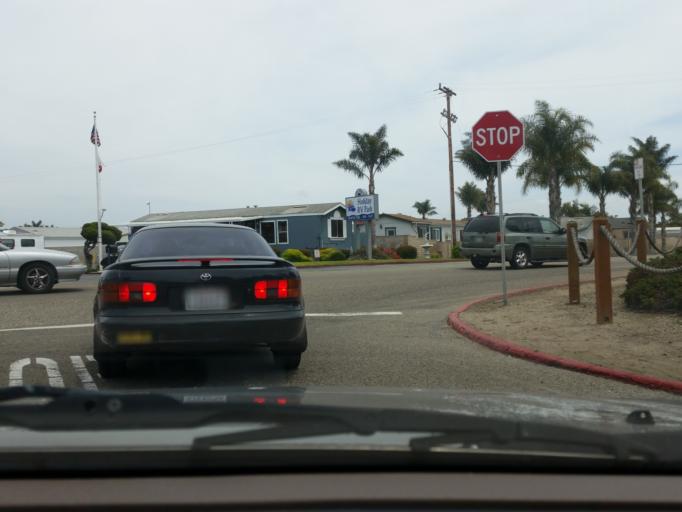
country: US
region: California
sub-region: San Luis Obispo County
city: Pismo Beach
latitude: 35.1363
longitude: -120.6381
